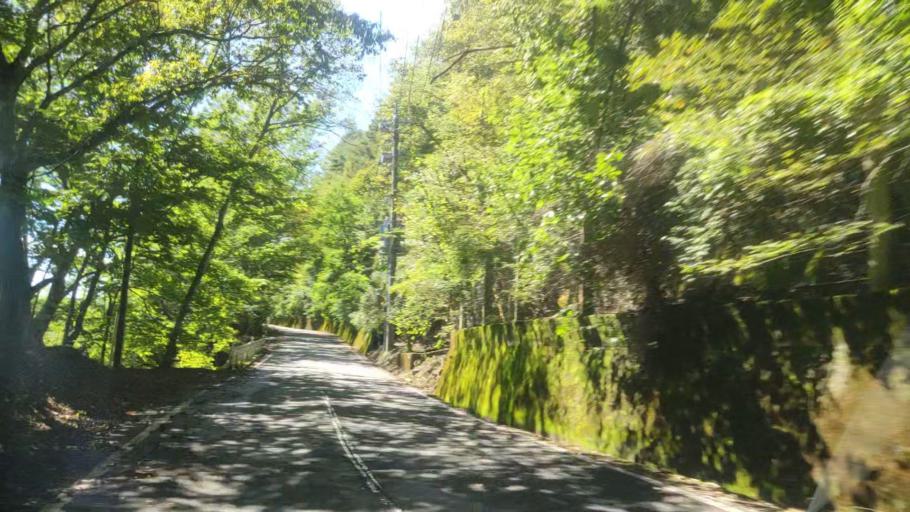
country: JP
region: Yamanashi
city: Fujikawaguchiko
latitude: 35.5562
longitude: 138.7912
